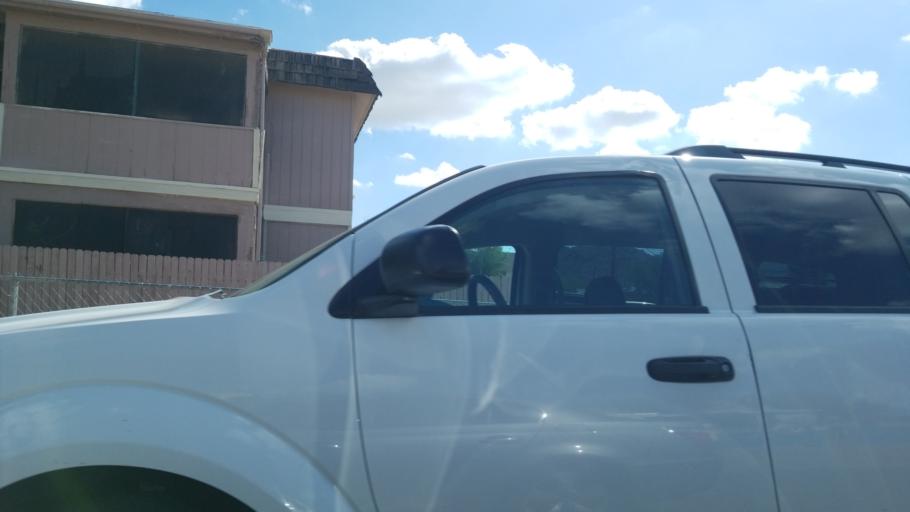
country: US
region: Arizona
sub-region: Maricopa County
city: Glendale
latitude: 33.5881
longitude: -112.0955
